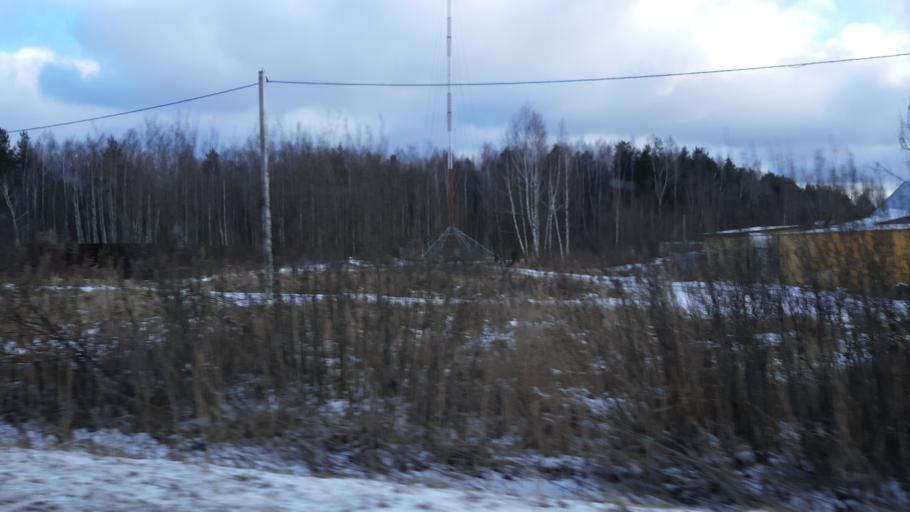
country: RU
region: Moskovskaya
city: Noginsk-9
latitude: 55.9979
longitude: 38.5450
